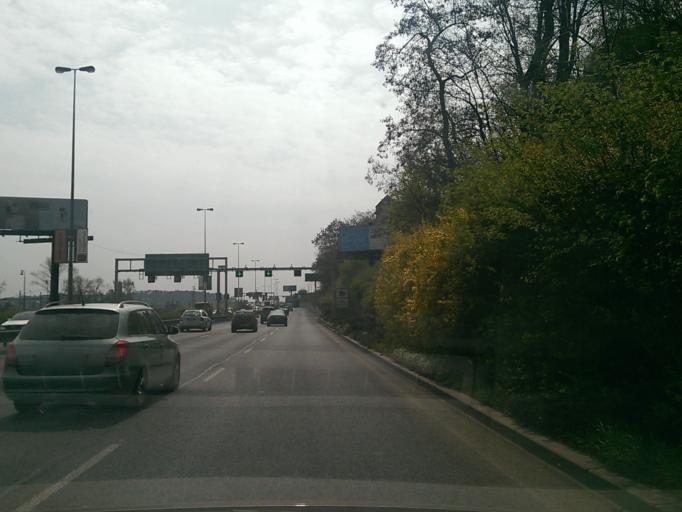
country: CZ
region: Praha
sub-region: Praha 2
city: Vysehrad
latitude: 50.0588
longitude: 14.4064
